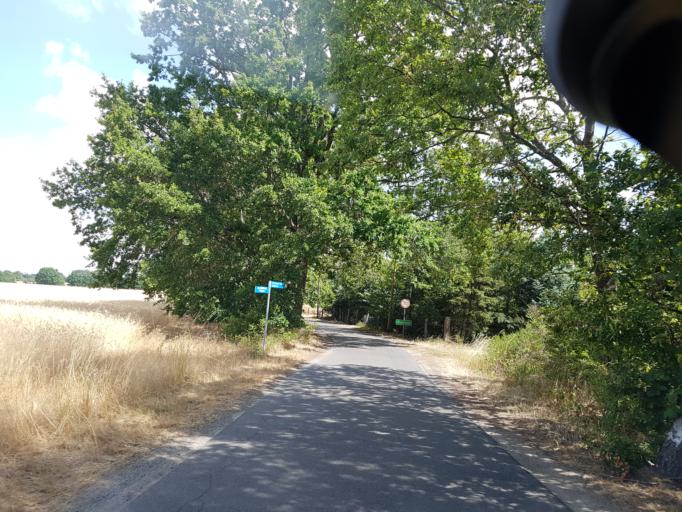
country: DE
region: Brandenburg
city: Cottbus
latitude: 51.6877
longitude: 14.3102
